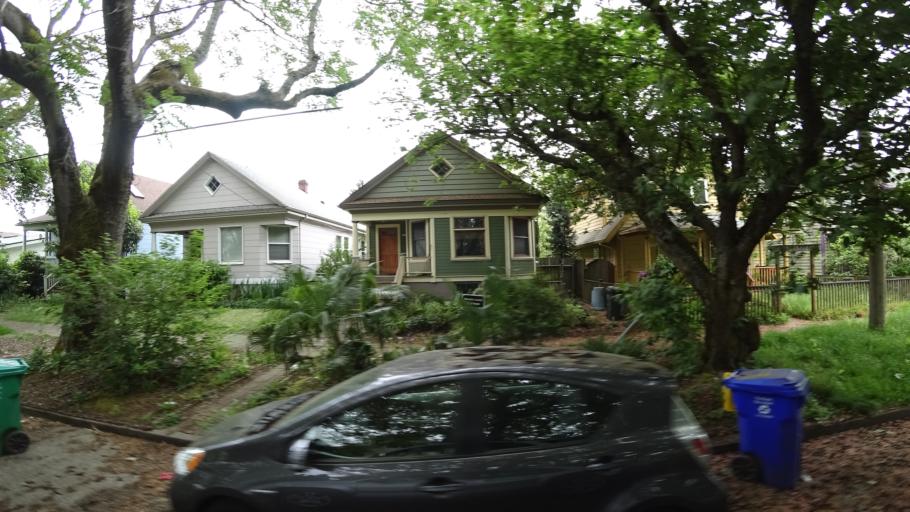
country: US
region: Oregon
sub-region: Multnomah County
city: Portland
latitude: 45.5572
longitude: -122.6701
